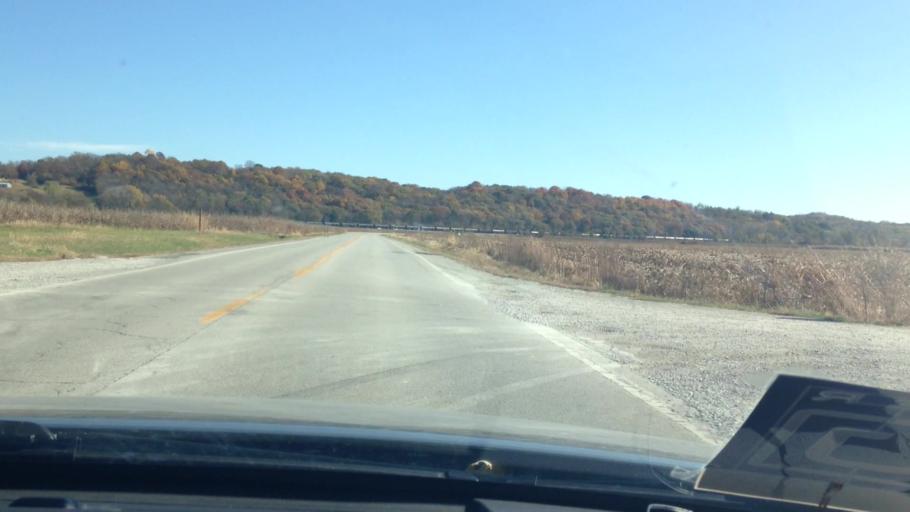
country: US
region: Kansas
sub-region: Leavenworth County
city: Leavenworth
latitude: 39.3246
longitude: -94.8656
